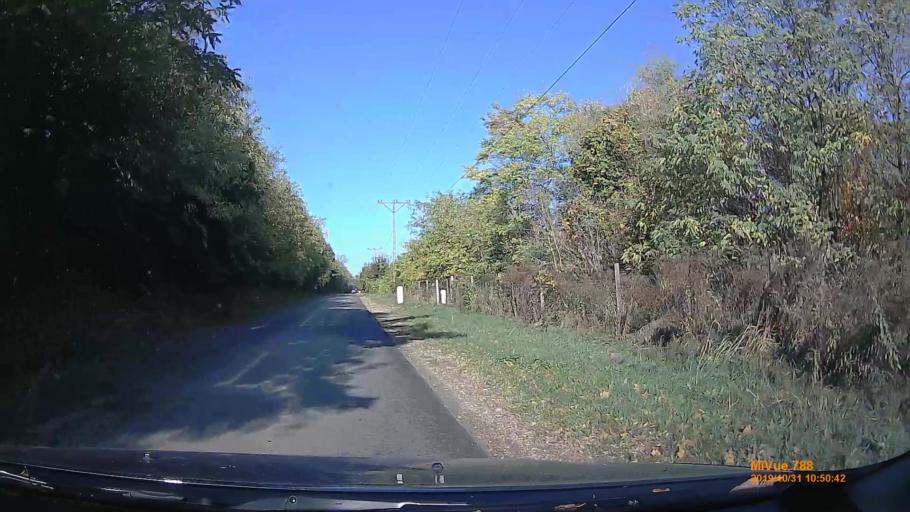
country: HU
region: Pest
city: Pilisborosjeno
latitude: 47.5989
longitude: 18.9971
